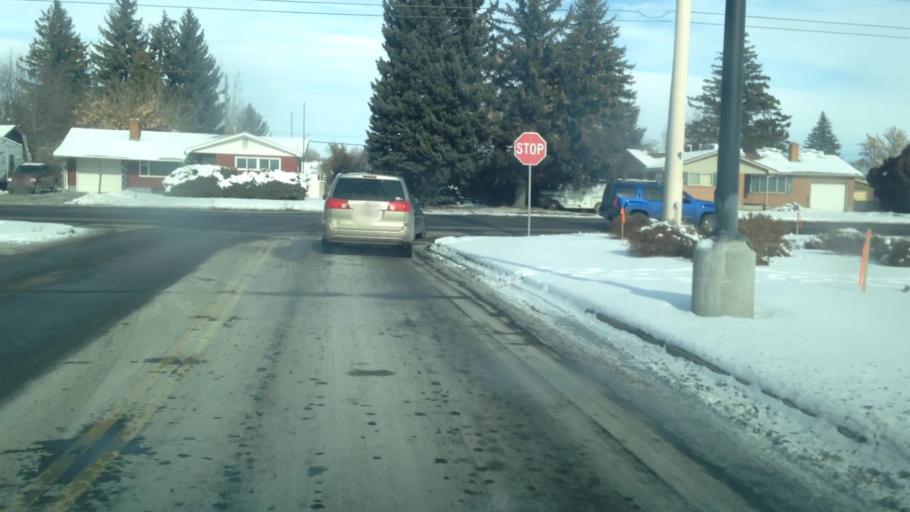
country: US
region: Idaho
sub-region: Bonneville County
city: Idaho Falls
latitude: 43.4821
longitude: -112.0195
